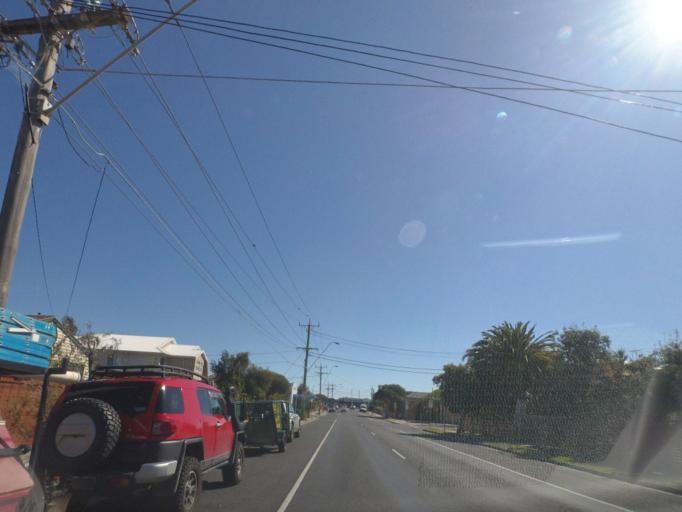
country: AU
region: Victoria
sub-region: Kingston
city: Edithvale
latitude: -38.0379
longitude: 145.1111
